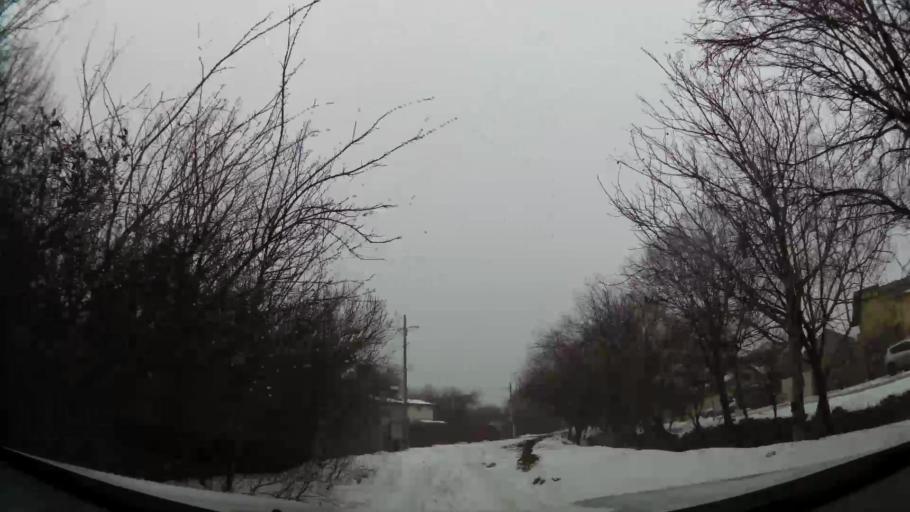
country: RO
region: Ilfov
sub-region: Comuna Chiajna
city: Rosu
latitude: 44.4430
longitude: 26.0127
